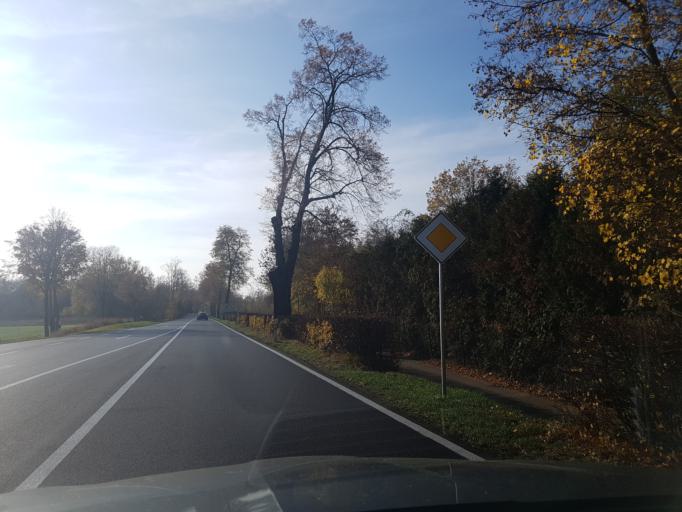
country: DE
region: Saxony
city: Torgau
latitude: 51.5628
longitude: 13.0203
